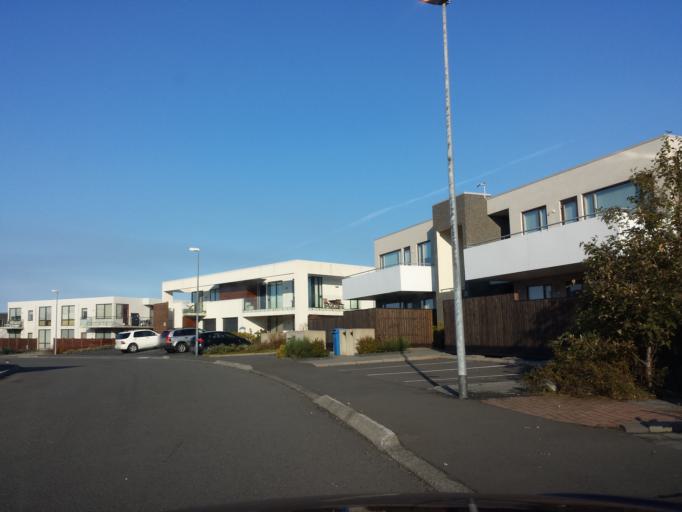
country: IS
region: Capital Region
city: Reykjavik
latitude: 64.0871
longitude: -21.8268
